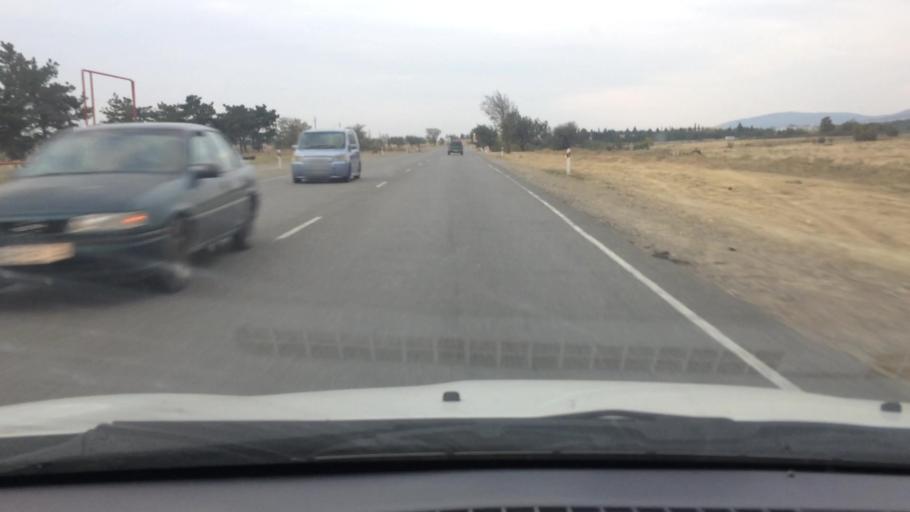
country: GE
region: T'bilisi
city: Tbilisi
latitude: 41.6401
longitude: 44.8814
